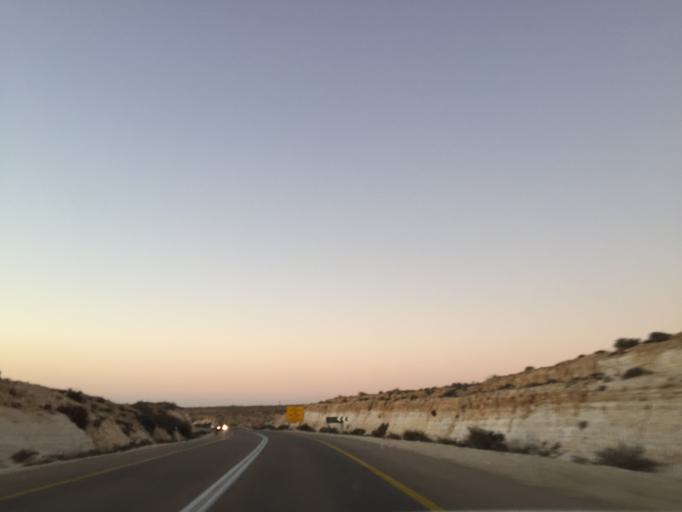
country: IL
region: Southern District
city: Midreshet Ben-Gurion
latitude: 30.8907
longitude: 34.7919
